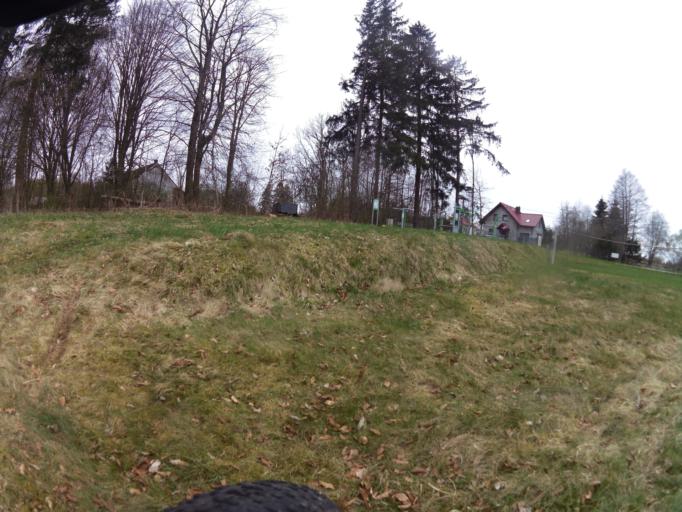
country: PL
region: West Pomeranian Voivodeship
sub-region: Powiat koszalinski
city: Polanow
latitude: 54.0991
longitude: 16.6101
